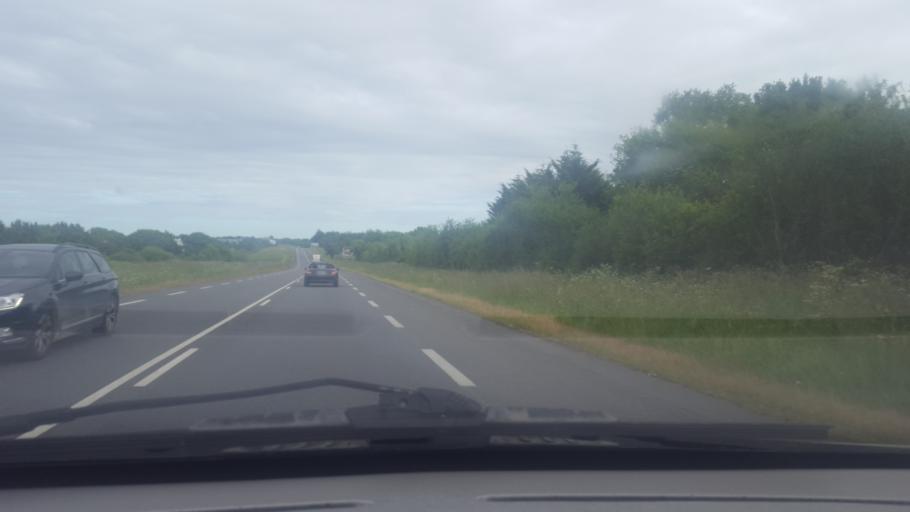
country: FR
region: Pays de la Loire
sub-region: Departement de la Loire-Atlantique
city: La Bernerie-en-Retz
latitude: 47.0844
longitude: -2.0232
